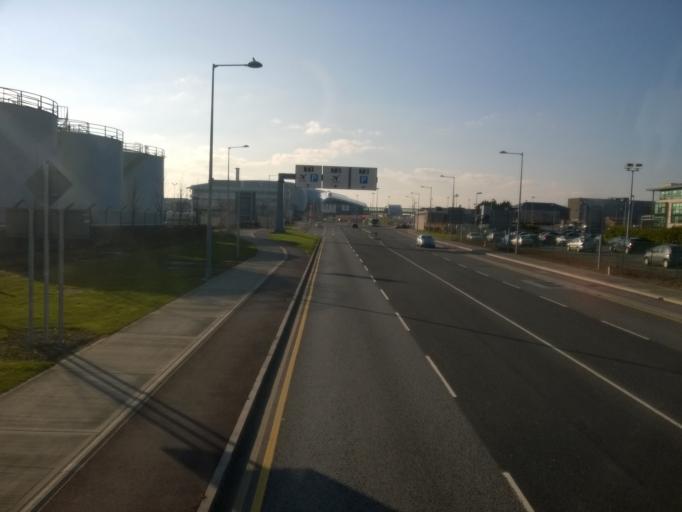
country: IE
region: Leinster
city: Beaumont
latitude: 53.4237
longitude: -6.2317
